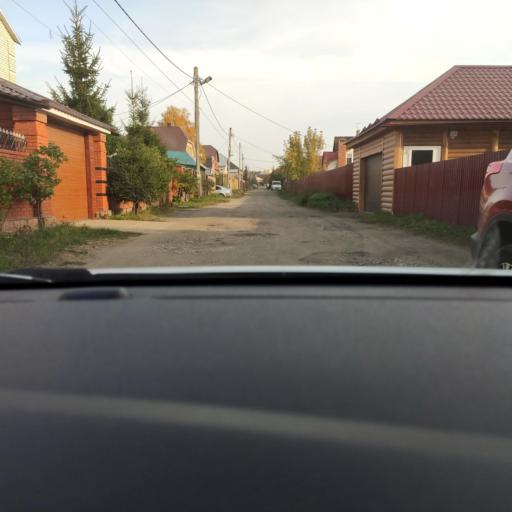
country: RU
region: Tatarstan
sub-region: Gorod Kazan'
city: Kazan
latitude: 55.8225
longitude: 49.2267
